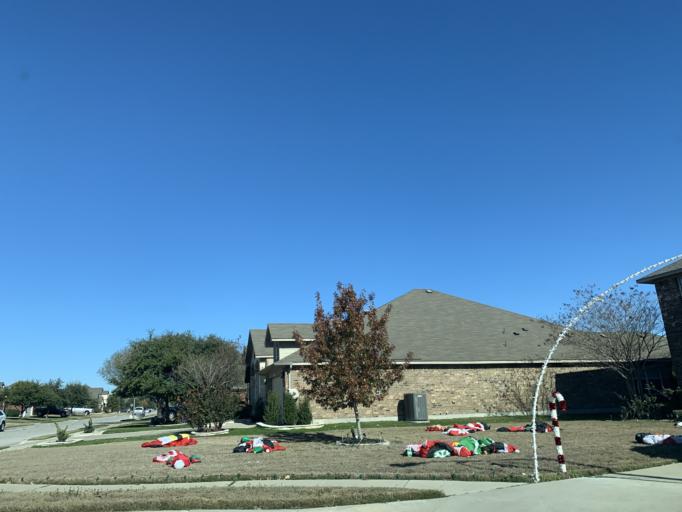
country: US
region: Texas
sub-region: Williamson County
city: Hutto
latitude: 30.5461
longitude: -97.5654
